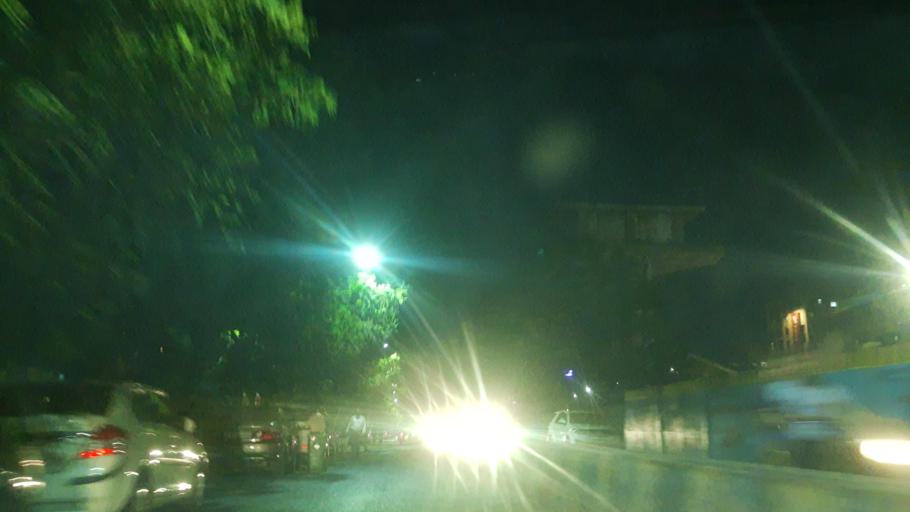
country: IN
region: Maharashtra
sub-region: Thane
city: Thane
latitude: 19.2067
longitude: 72.9706
